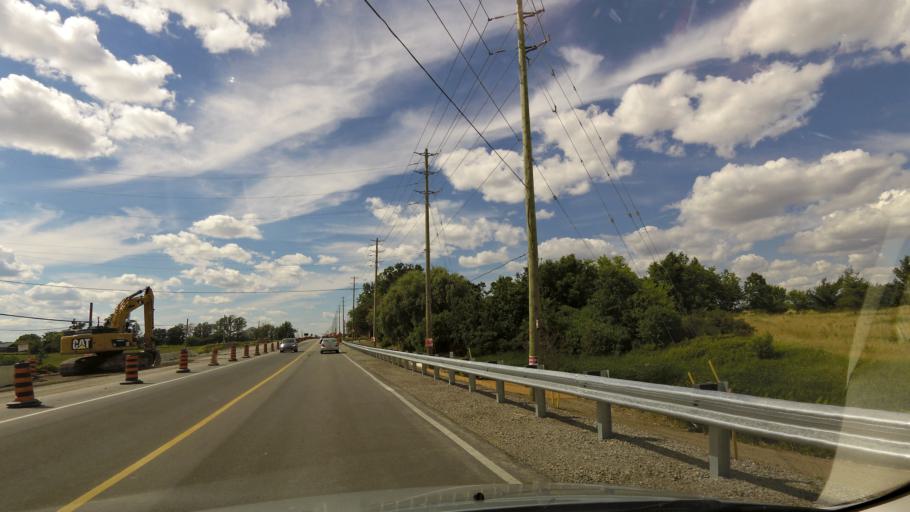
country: CA
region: Ontario
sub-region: Halton
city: Milton
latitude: 43.4786
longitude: -79.8233
